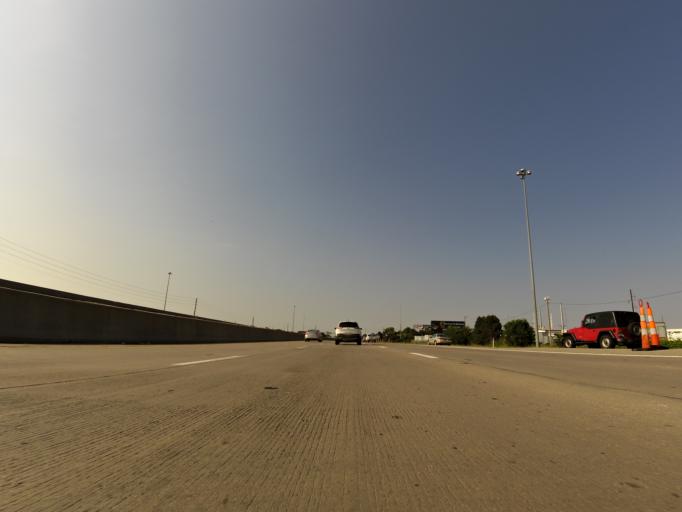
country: US
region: Kansas
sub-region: Sedgwick County
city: Park City
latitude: 37.7454
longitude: -97.3189
